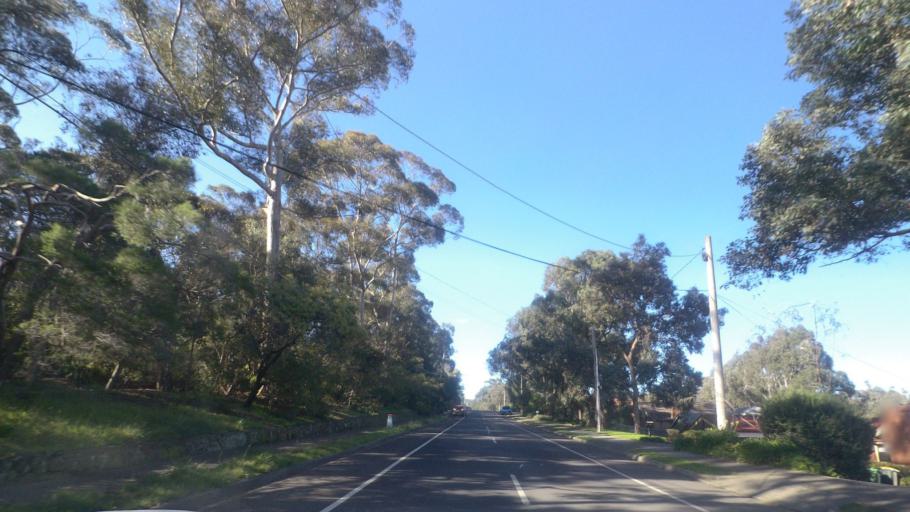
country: AU
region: Victoria
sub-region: Nillumbik
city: Eltham
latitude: -37.7217
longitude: 145.1530
